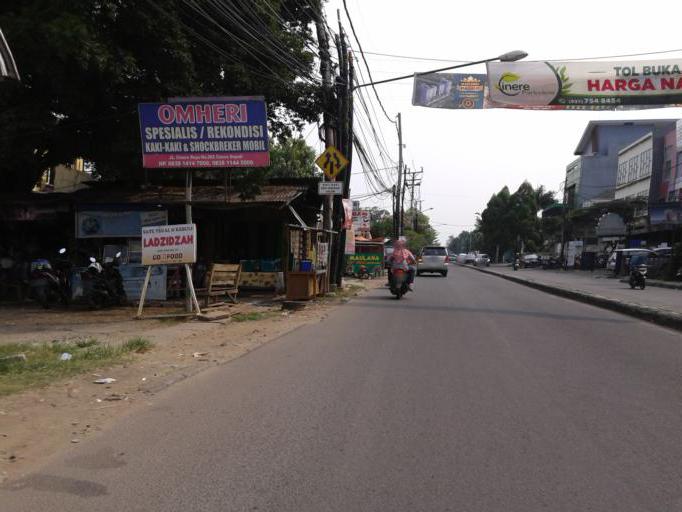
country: ID
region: West Java
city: Pamulang
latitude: -6.3403
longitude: 106.7799
